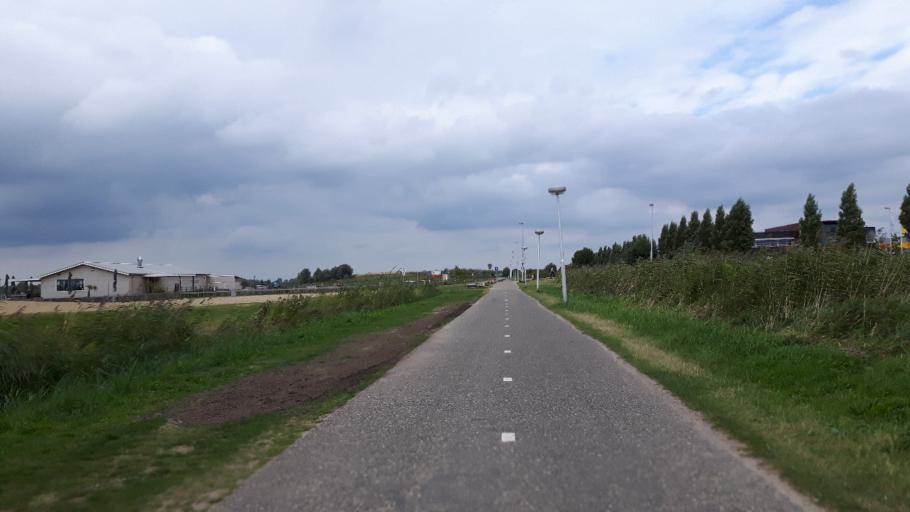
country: NL
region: Utrecht
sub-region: Stichtse Vecht
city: Spechtenkamp
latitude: 52.1173
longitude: 5.0275
